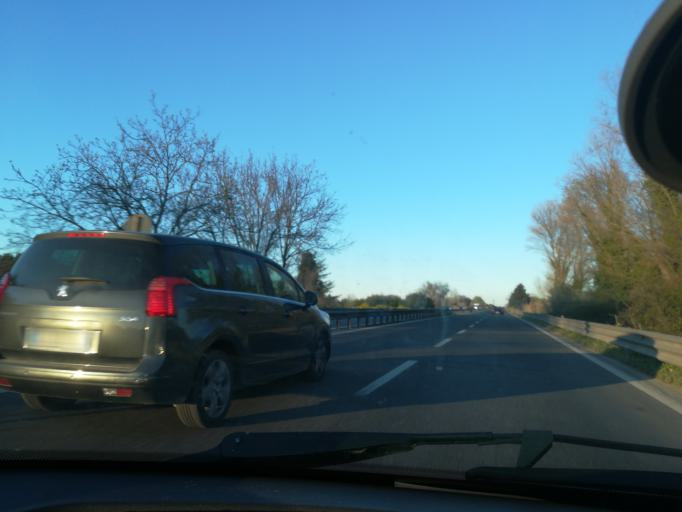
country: IT
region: The Marches
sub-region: Provincia di Macerata
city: Santa Maria Apparente
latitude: 43.2829
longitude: 13.6927
